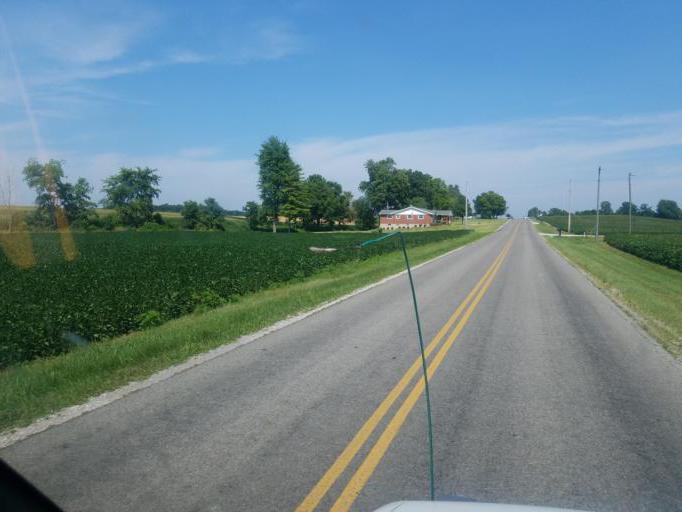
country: US
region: Ohio
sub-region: Shelby County
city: Botkins
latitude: 40.4972
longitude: -84.1345
